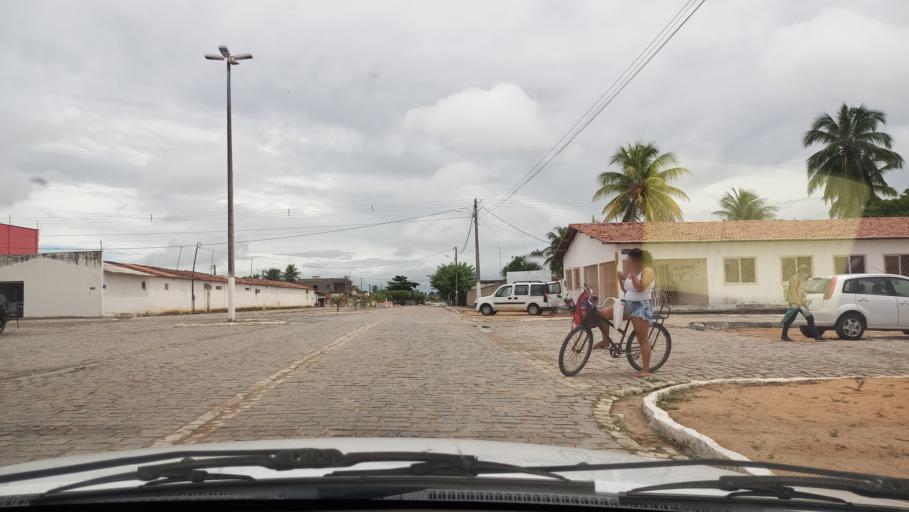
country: BR
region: Rio Grande do Norte
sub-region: Poco Branco
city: Poco Branco
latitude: -5.6184
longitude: -35.6567
